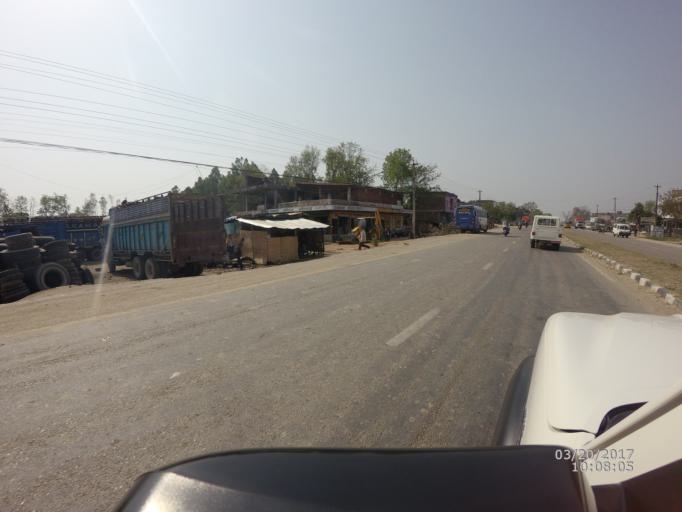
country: NP
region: Mid Western
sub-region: Bheri Zone
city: Nepalgunj
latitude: 28.0841
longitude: 81.6457
